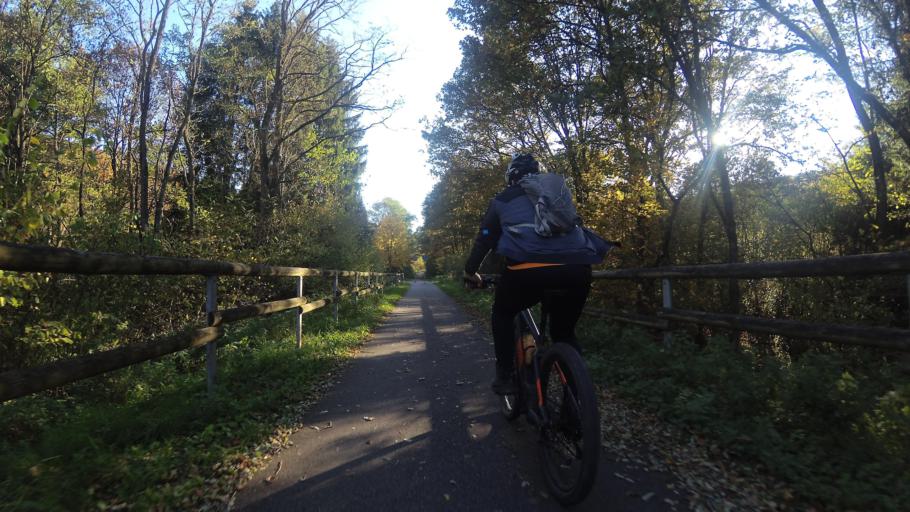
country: DE
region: Rheinland-Pfalz
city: Gutweiler
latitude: 49.7251
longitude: 6.7364
